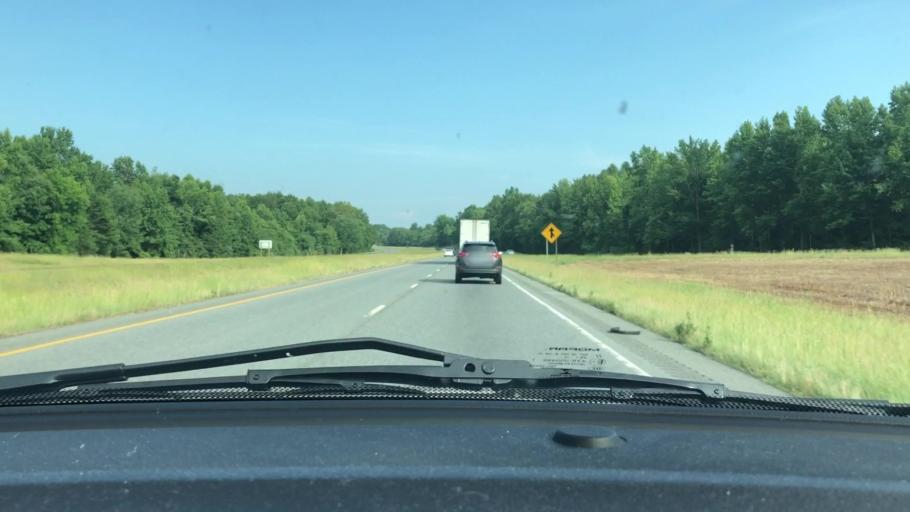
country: US
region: North Carolina
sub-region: Randolph County
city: Liberty
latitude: 35.8473
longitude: -79.6046
